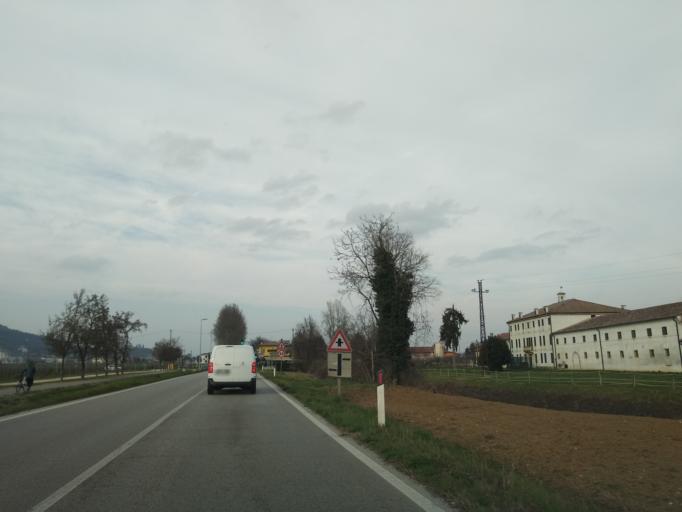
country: IT
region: Veneto
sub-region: Provincia di Vicenza
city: Lumignano
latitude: 45.4526
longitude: 11.6020
